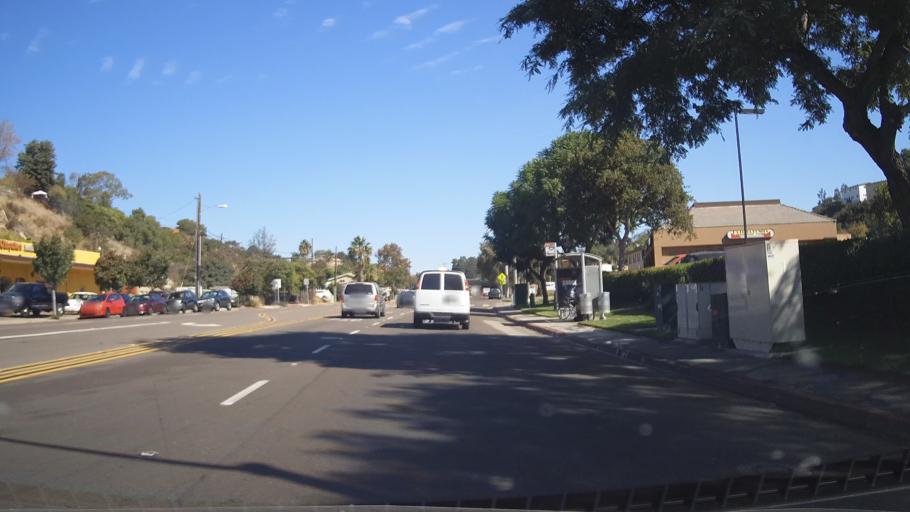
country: US
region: California
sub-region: San Diego County
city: National City
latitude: 32.7232
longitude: -117.1075
